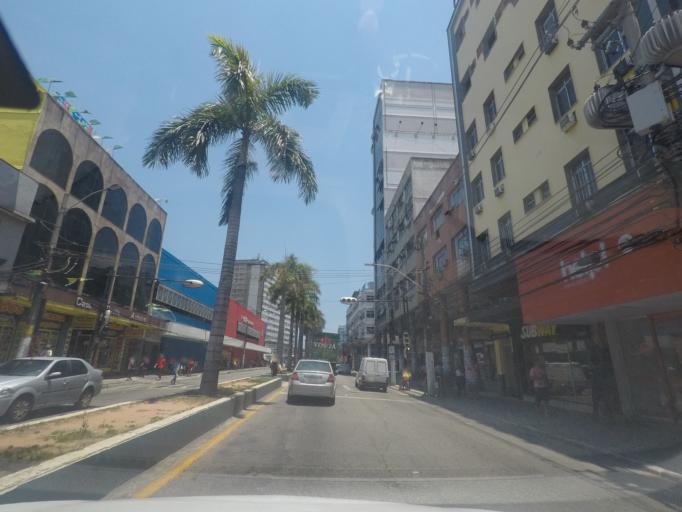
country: BR
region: Rio de Janeiro
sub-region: Duque De Caxias
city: Duque de Caxias
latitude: -22.7905
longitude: -43.3099
